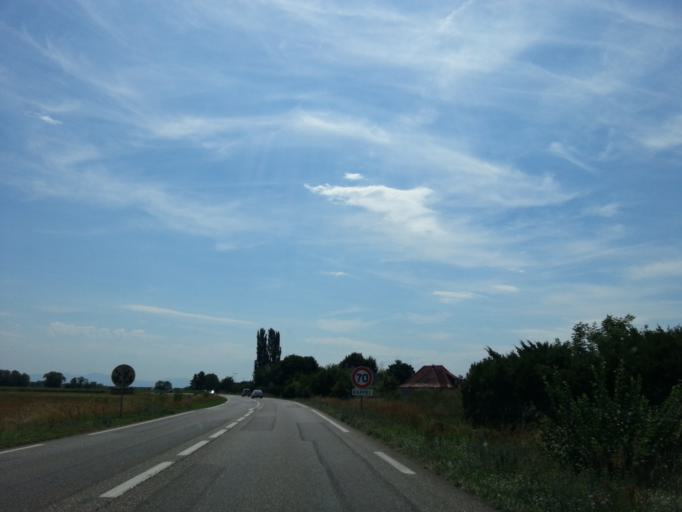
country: FR
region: Alsace
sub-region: Departement du Haut-Rhin
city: Andolsheim
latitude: 48.0624
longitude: 7.4222
